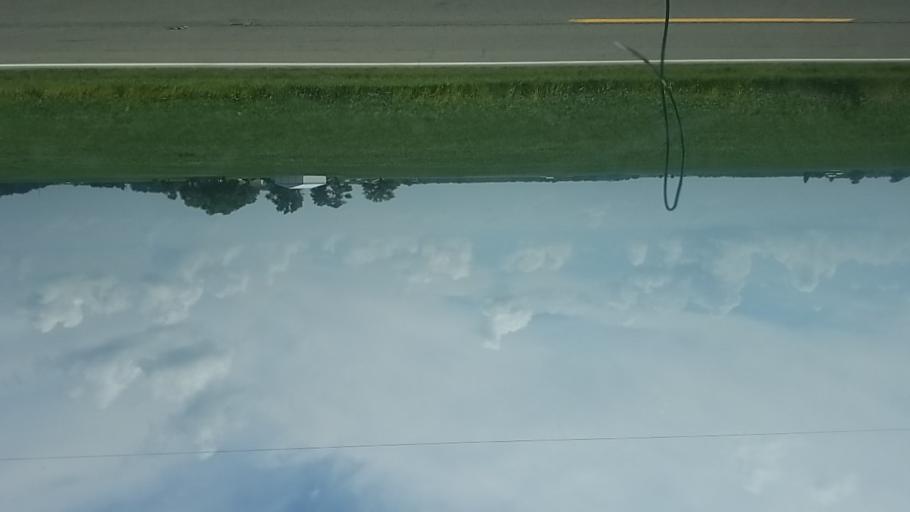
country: US
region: Ohio
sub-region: Hardin County
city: Kenton
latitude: 40.6998
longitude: -83.5762
